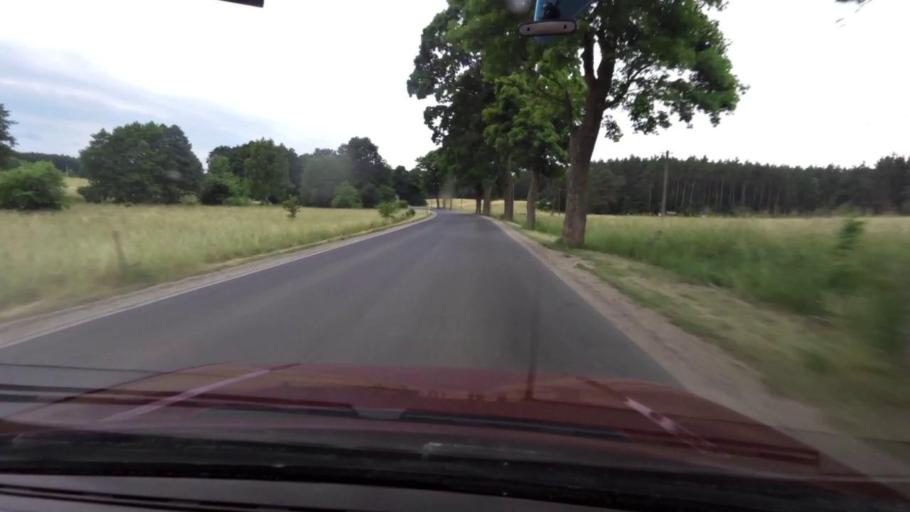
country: PL
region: West Pomeranian Voivodeship
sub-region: Powiat koszalinski
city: Sianow
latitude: 54.1688
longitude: 16.4285
